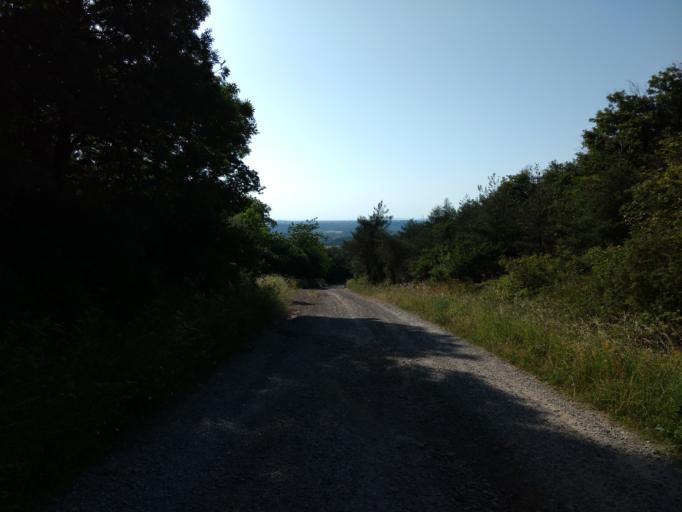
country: FR
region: Midi-Pyrenees
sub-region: Departement de l'Aveyron
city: La Loubiere
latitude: 44.3640
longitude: 2.7012
